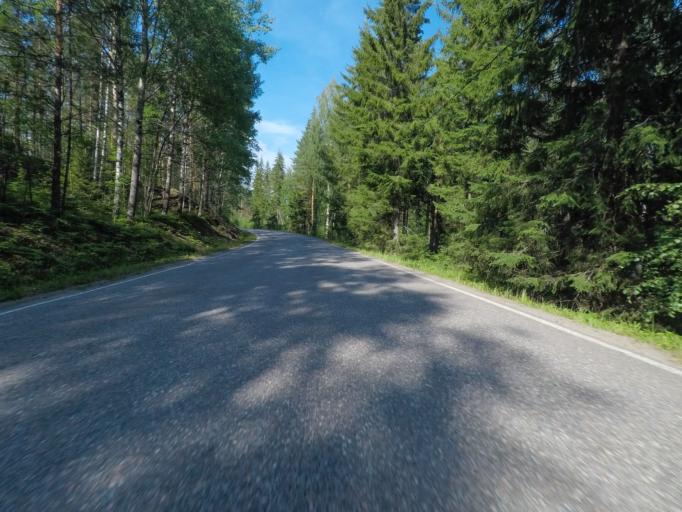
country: FI
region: Southern Savonia
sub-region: Mikkeli
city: Puumala
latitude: 61.6092
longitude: 28.2202
